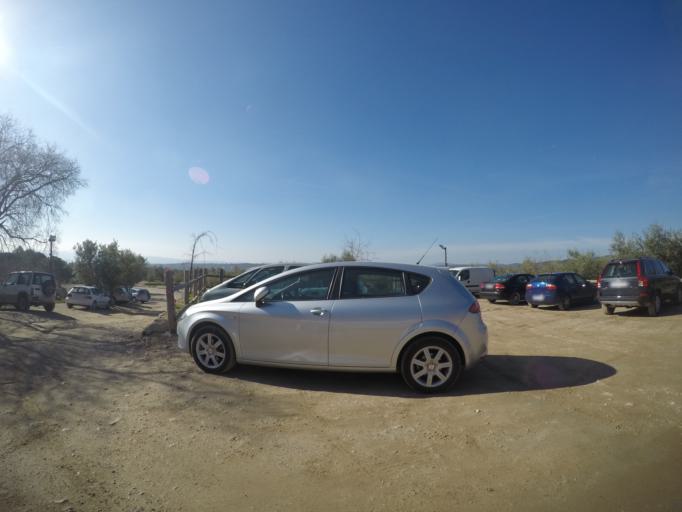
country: ES
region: Catalonia
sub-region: Provincia de Barcelona
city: Collbato
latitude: 41.5826
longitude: 1.8091
